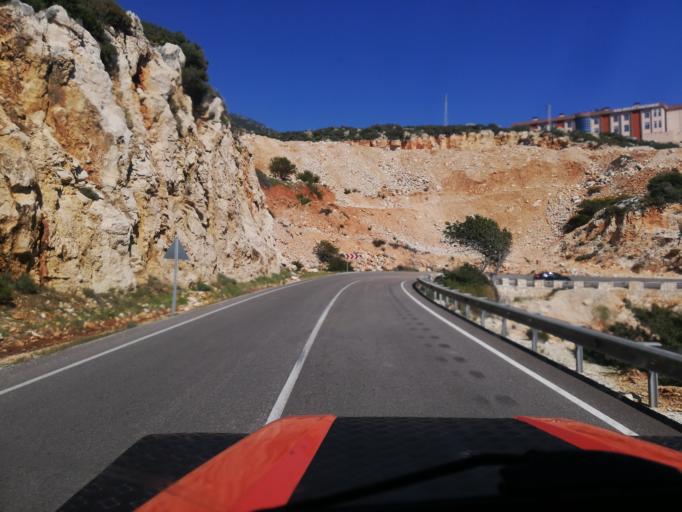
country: TR
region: Antalya
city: Kas
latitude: 36.2031
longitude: 29.5831
